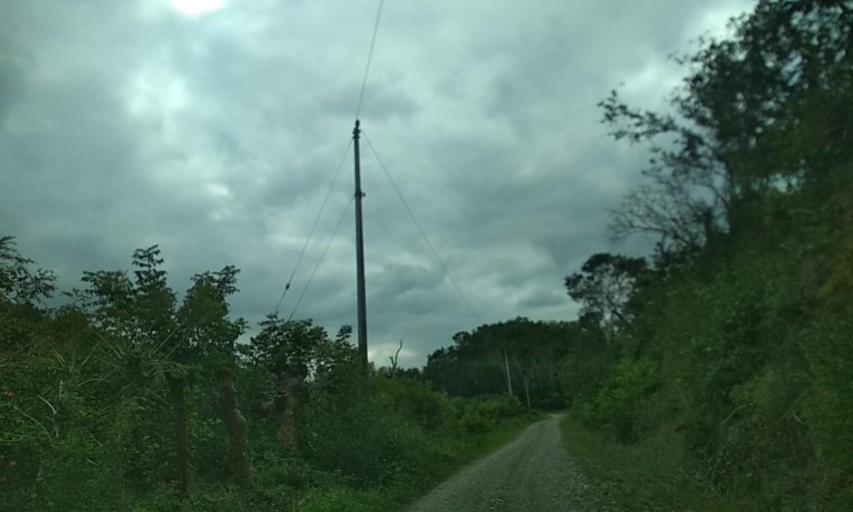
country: MX
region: Veracruz
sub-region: Papantla
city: Polutla
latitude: 20.5257
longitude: -97.2979
